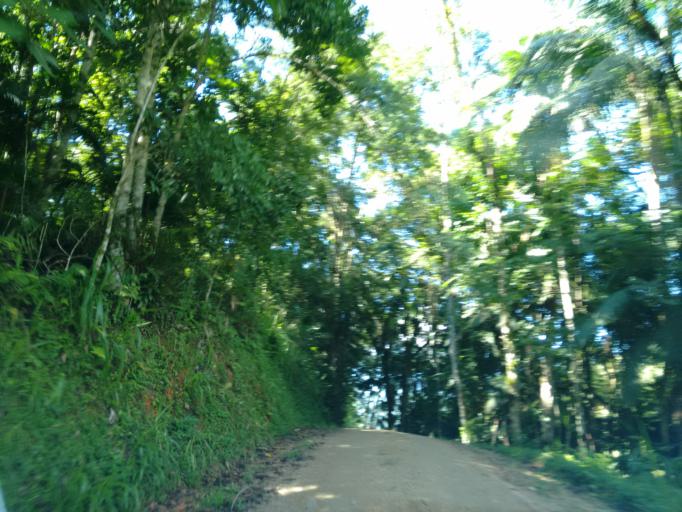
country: BR
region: Santa Catarina
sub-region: Pomerode
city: Pomerode
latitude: -26.7536
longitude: -49.1941
